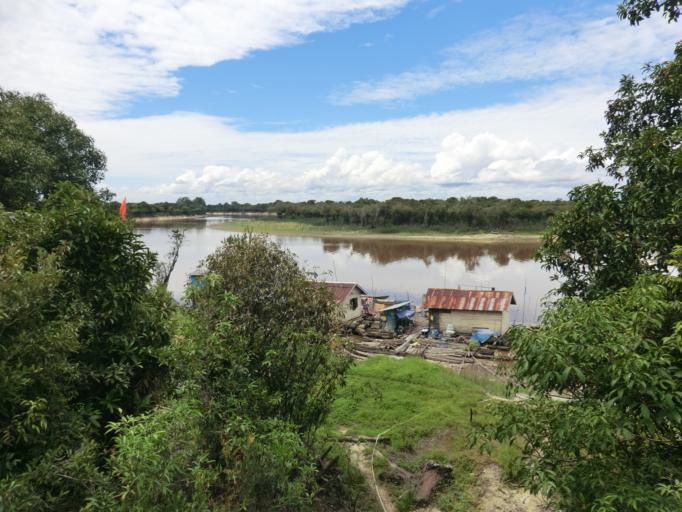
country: MY
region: Sarawak
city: Simanggang
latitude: 0.8391
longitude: 112.0639
